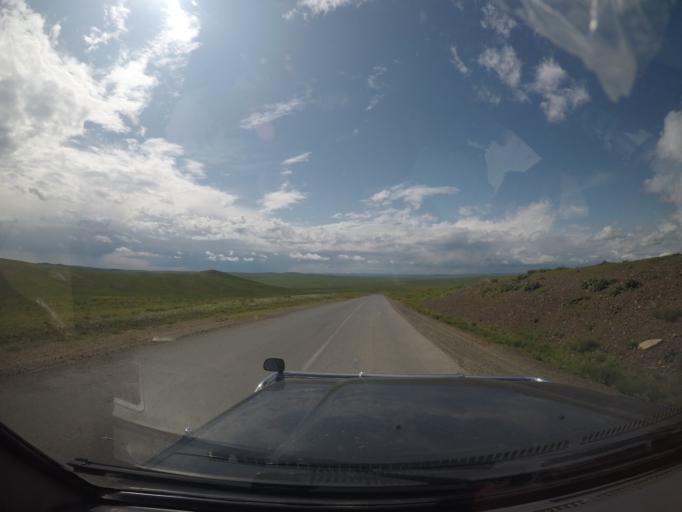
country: MN
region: Hentiy
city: Bayanbulag
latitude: 47.4431
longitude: 109.7637
